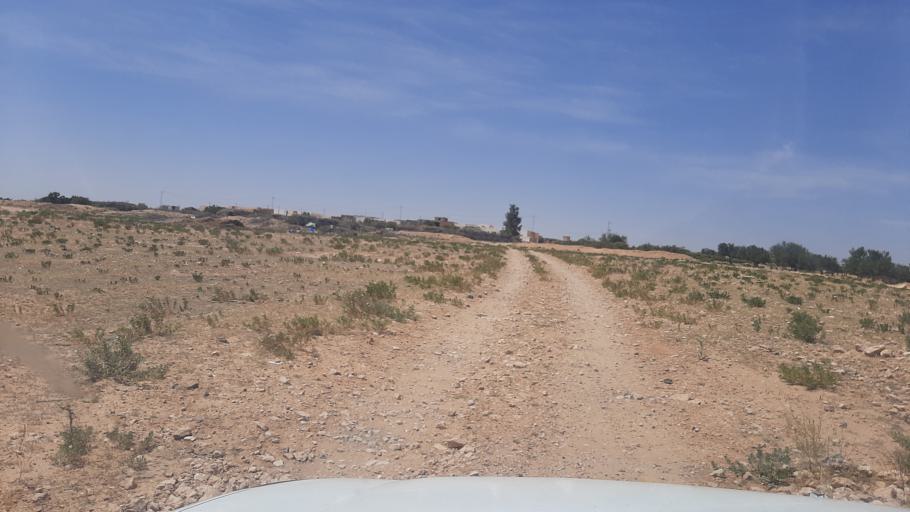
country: TN
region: Safaqis
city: Bi'r `Ali Bin Khalifah
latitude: 34.5645
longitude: 10.3464
